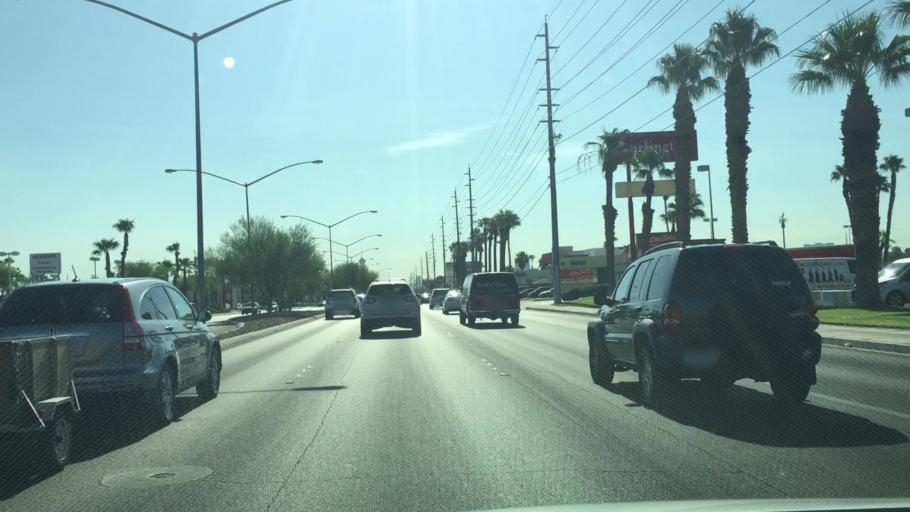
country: US
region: Nevada
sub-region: Clark County
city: Spring Valley
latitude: 36.1442
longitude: -115.2240
